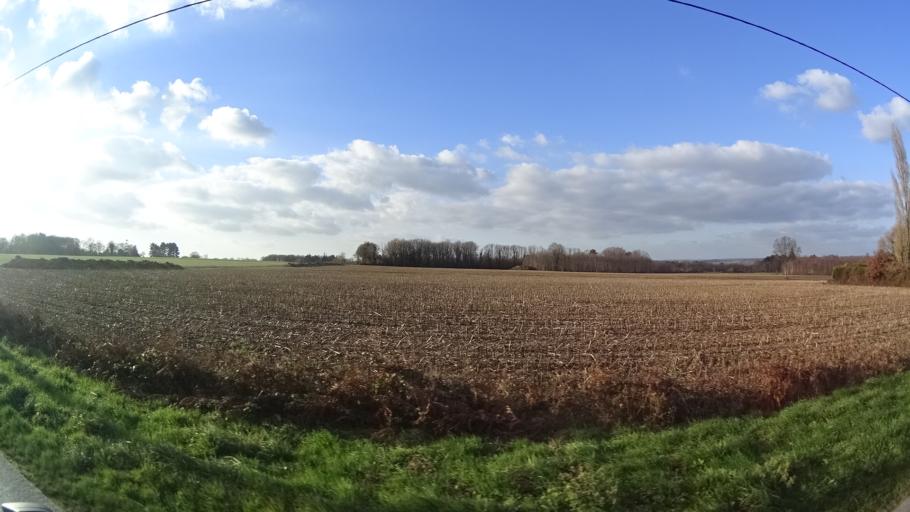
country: FR
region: Pays de la Loire
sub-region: Departement de la Loire-Atlantique
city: Guemene-Penfao
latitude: 47.6059
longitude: -1.8435
